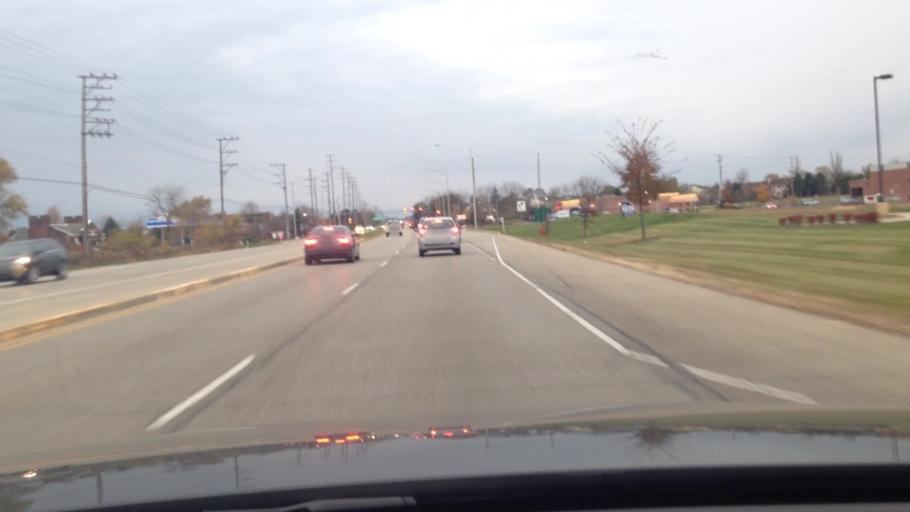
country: US
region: Illinois
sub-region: McHenry County
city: Lake in the Hills
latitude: 42.1758
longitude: -88.3793
